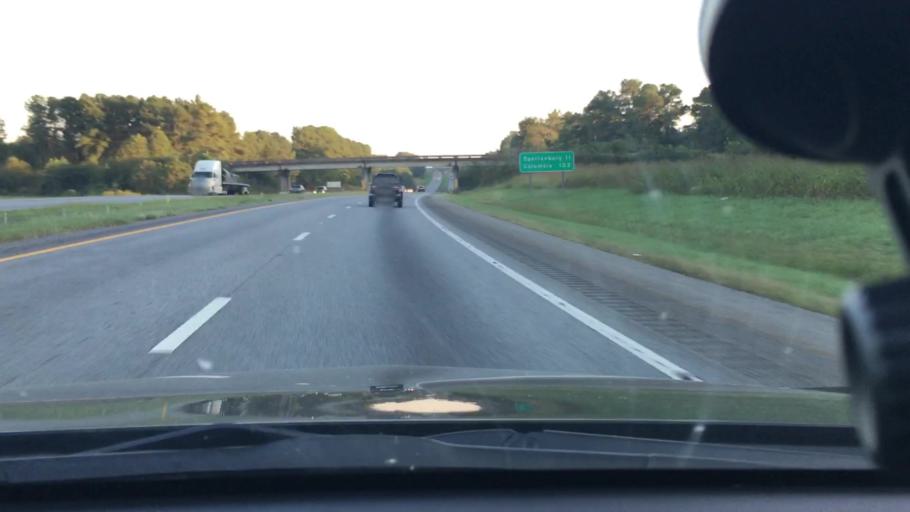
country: US
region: South Carolina
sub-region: Spartanburg County
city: Inman
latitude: 35.0721
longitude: -82.0539
